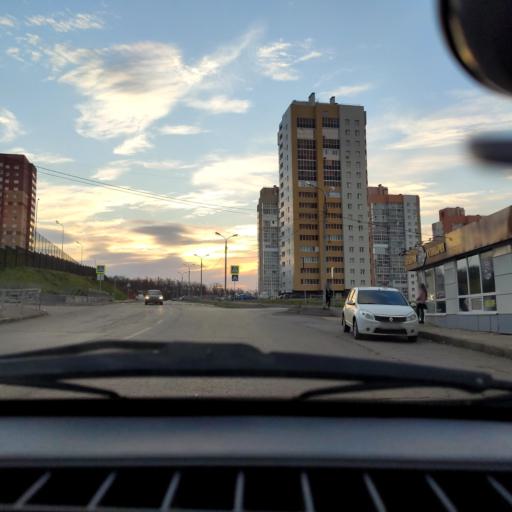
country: RU
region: Bashkortostan
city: Ufa
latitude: 54.6893
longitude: 55.9939
